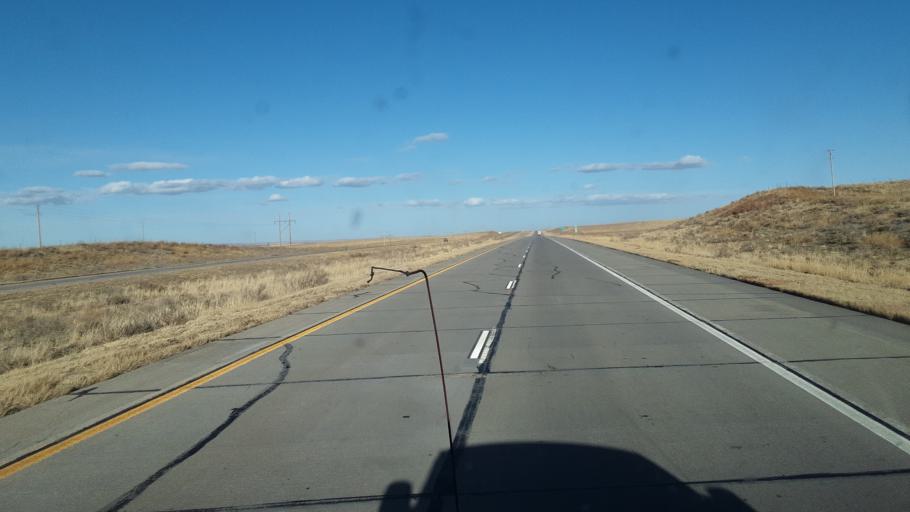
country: US
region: Colorado
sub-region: Logan County
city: Sterling
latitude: 40.6952
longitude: -103.0788
